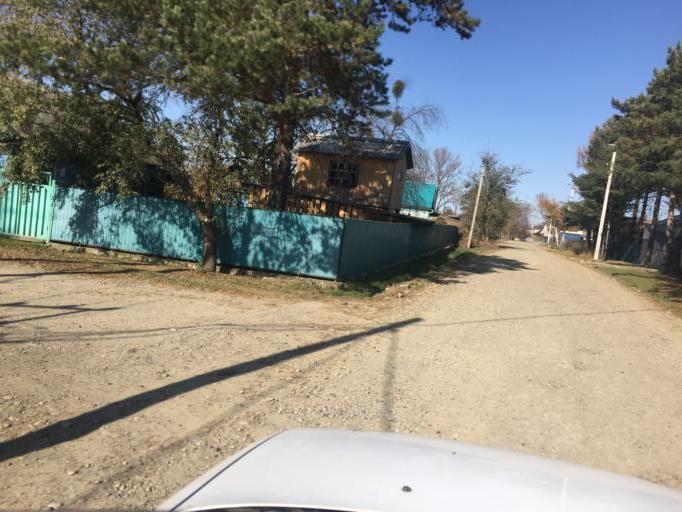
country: RU
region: Primorskiy
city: Dal'nerechensk
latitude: 45.9281
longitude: 133.7531
